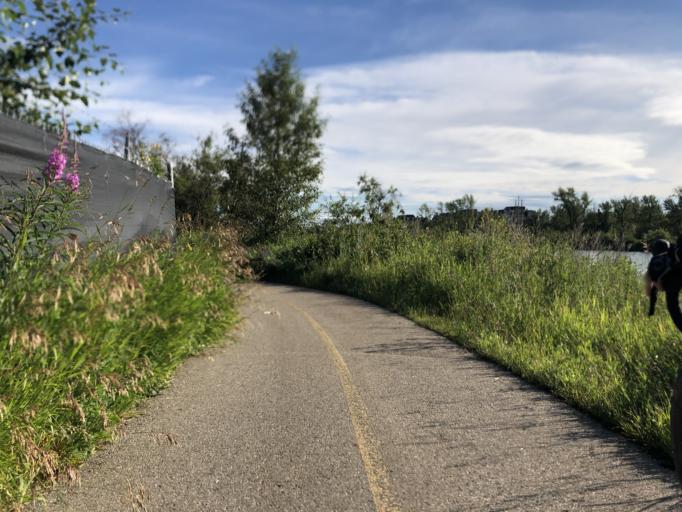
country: CA
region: Alberta
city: Calgary
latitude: 50.9589
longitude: -114.0246
